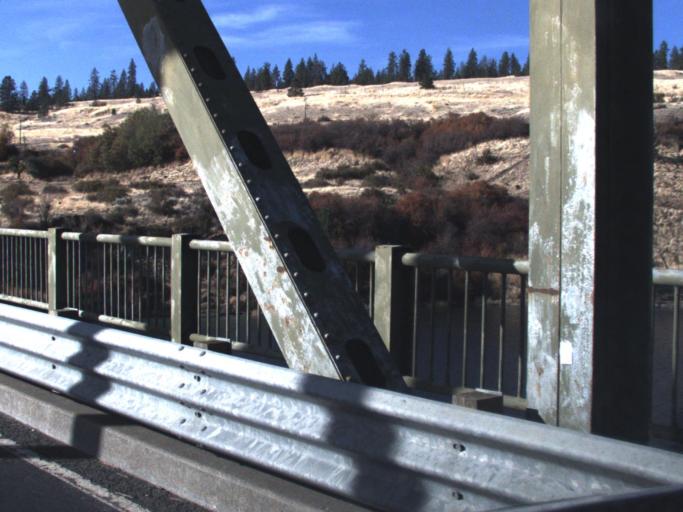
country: US
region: Washington
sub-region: Lincoln County
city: Davenport
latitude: 47.9081
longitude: -118.3175
